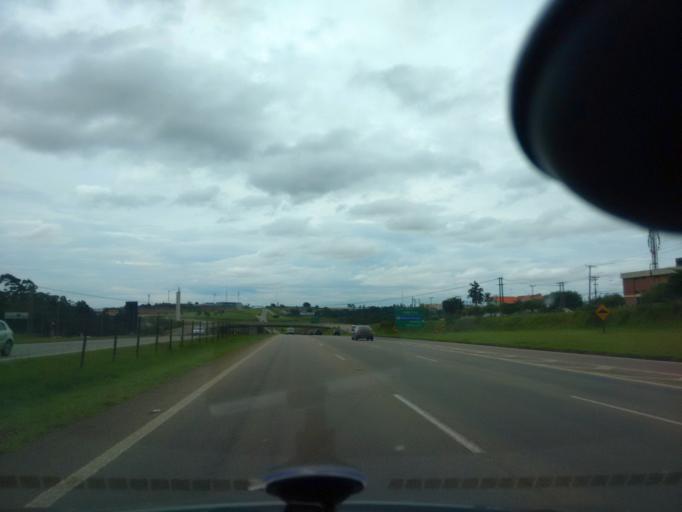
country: BR
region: Sao Paulo
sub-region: Campinas
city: Campinas
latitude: -23.0018
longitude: -47.1114
